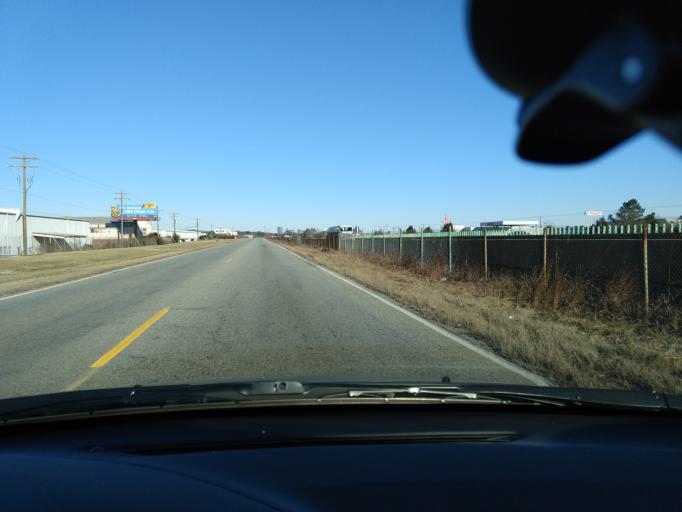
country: US
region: Virginia
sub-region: Chesterfield County
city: Bensley
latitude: 37.4829
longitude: -77.4316
